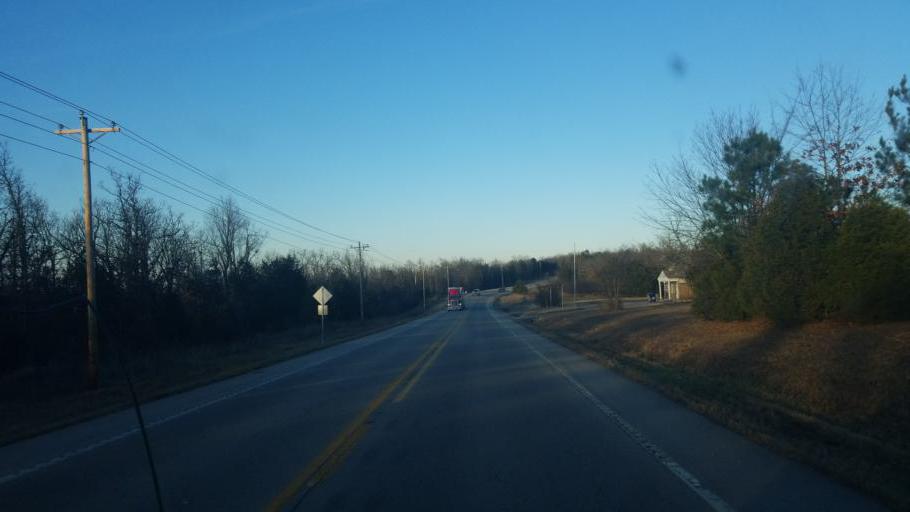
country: US
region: Arkansas
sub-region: Baxter County
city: Mountain Home
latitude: 36.3825
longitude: -92.1918
